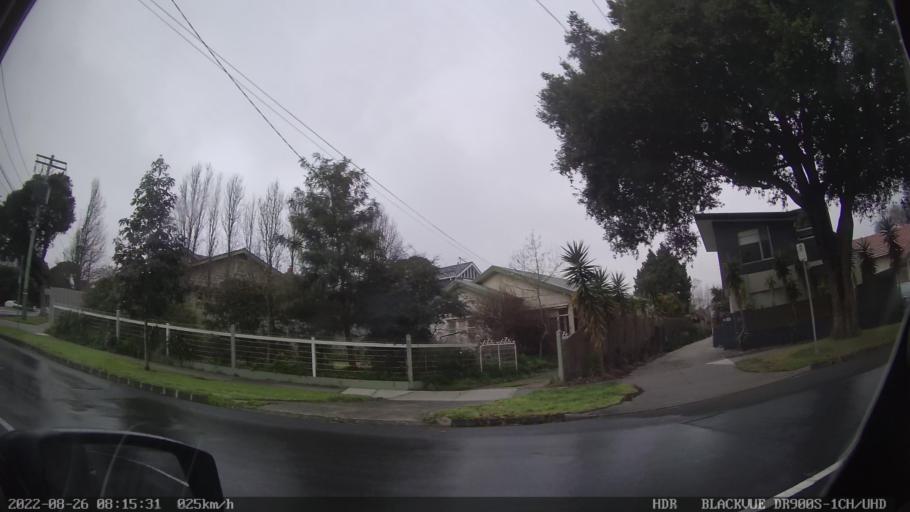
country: AU
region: Victoria
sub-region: Glen Eira
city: Elsternwick
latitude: -37.8925
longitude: 145.0086
